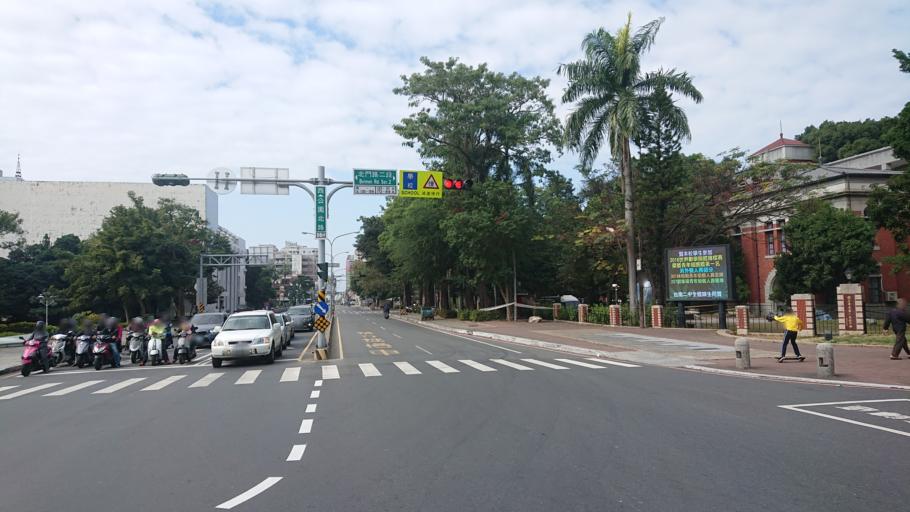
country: TW
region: Taiwan
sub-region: Tainan
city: Tainan
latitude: 23.0041
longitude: 120.2135
